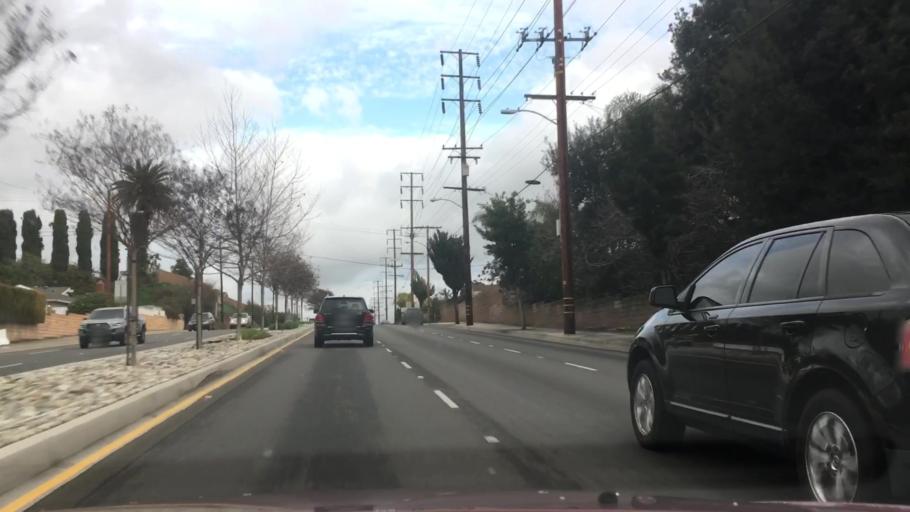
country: US
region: California
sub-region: Los Angeles County
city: East La Mirada
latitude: 33.9173
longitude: -117.9778
